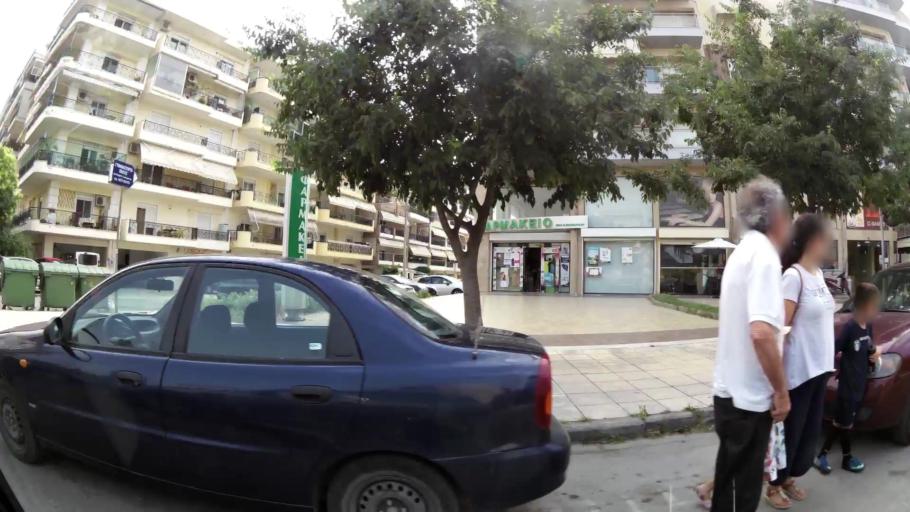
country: GR
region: Central Macedonia
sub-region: Nomos Thessalonikis
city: Stavroupoli
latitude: 40.6804
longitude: 22.9330
